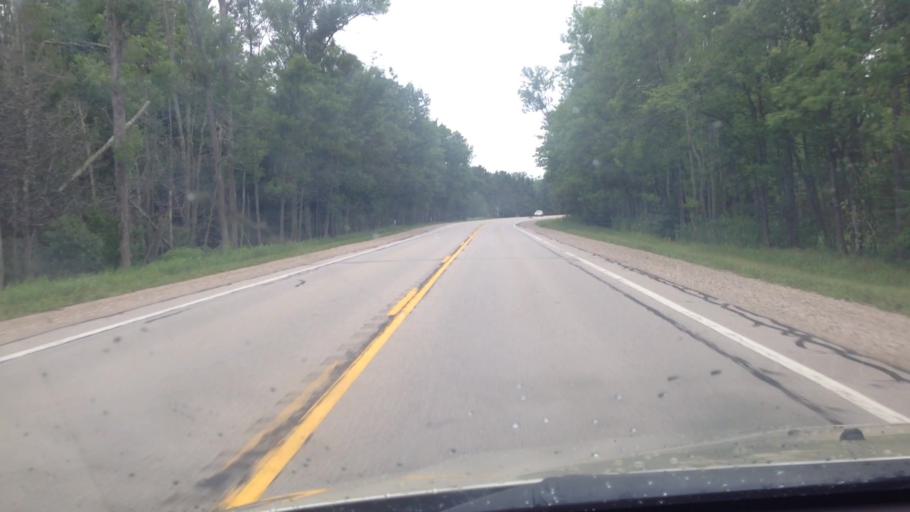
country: US
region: Michigan
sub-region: Menominee County
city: Menominee
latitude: 45.4240
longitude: -87.3497
